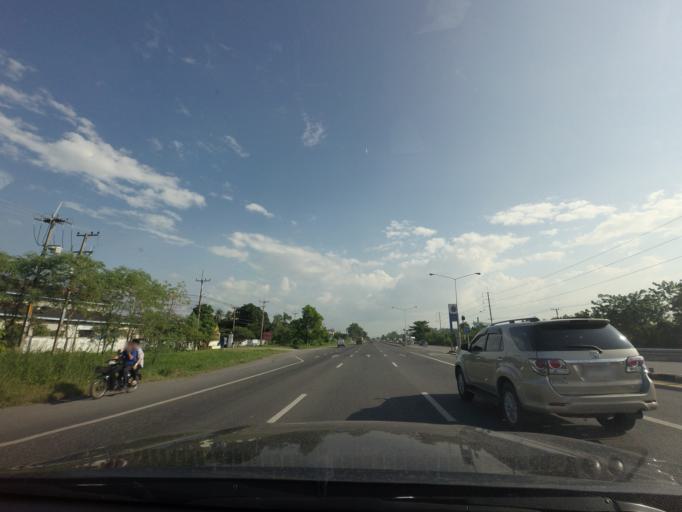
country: TH
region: Sara Buri
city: Chaloem Phra Kiat
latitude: 14.6369
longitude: 100.8877
